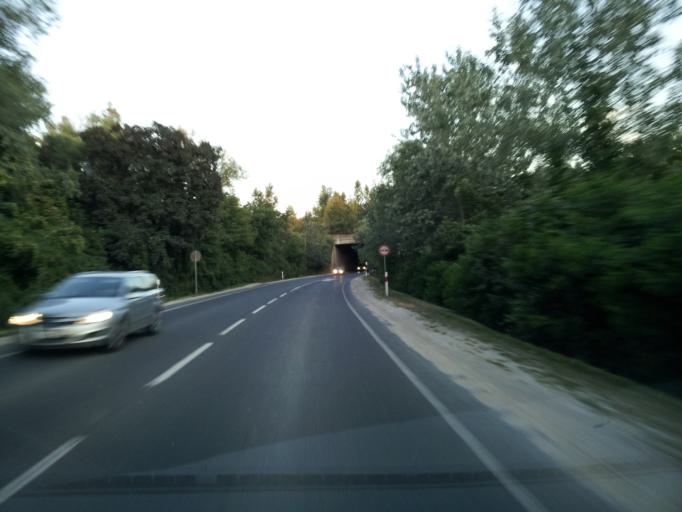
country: HU
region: Komarom-Esztergom
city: Tatabanya
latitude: 47.5620
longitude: 18.4470
